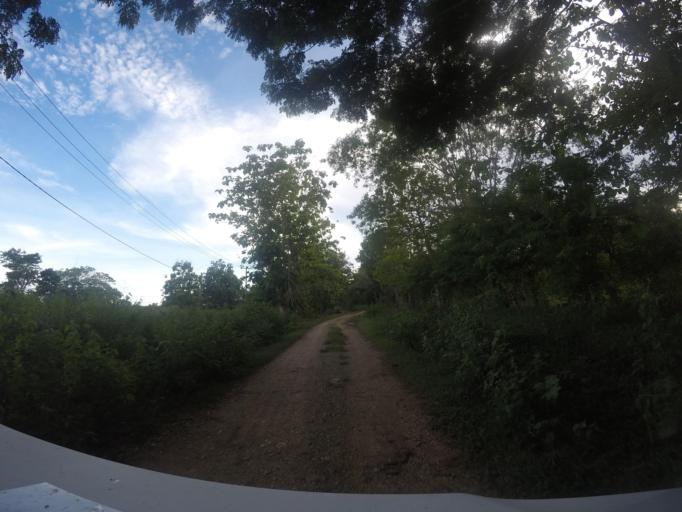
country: TL
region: Lautem
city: Lospalos
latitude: -8.5097
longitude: 126.9933
